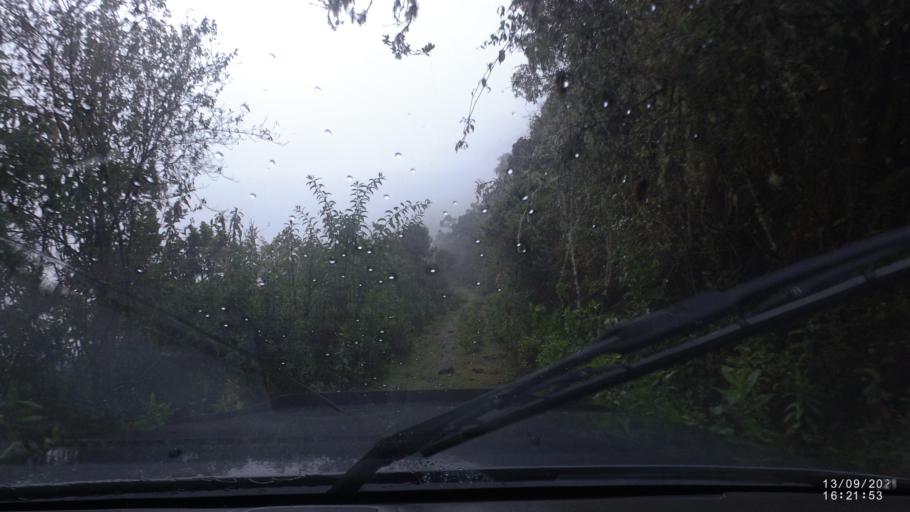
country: BO
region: Cochabamba
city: Colomi
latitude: -17.2683
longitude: -65.7014
